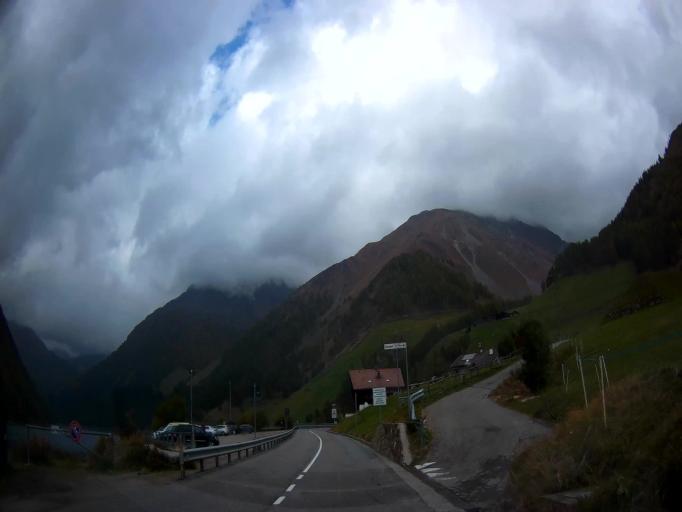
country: IT
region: Trentino-Alto Adige
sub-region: Bolzano
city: Senales
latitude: 46.7348
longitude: 10.8503
